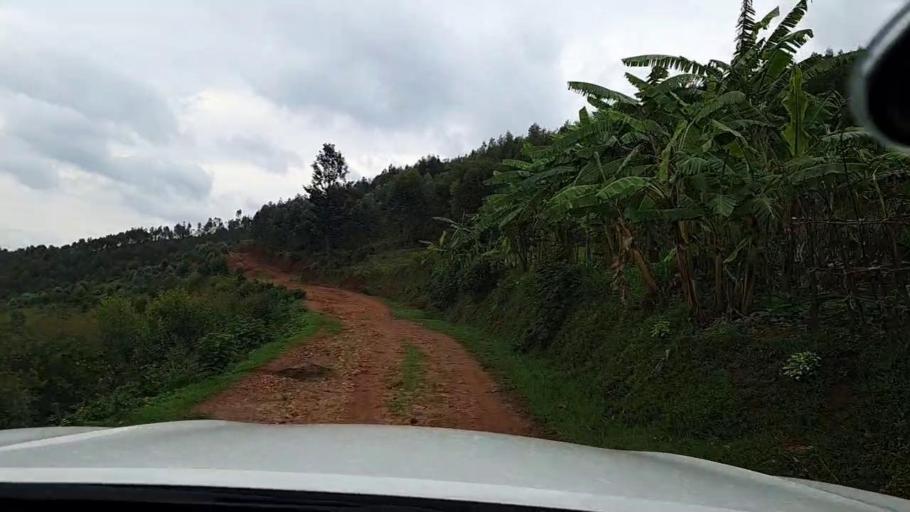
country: RW
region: Western Province
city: Kibuye
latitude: -2.1897
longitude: 29.2998
